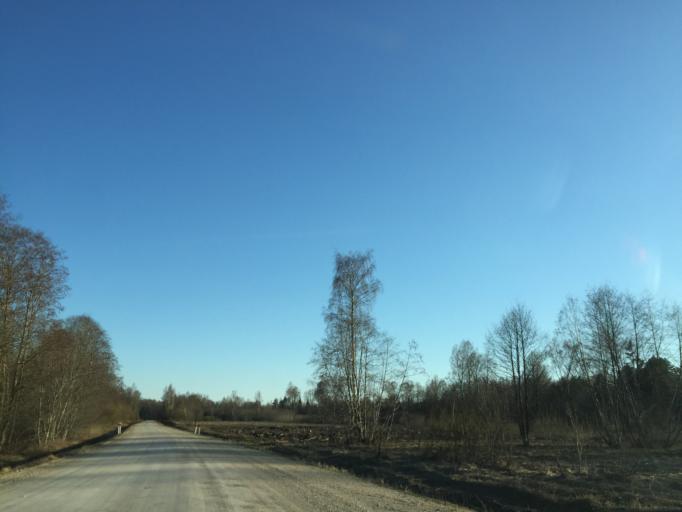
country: EE
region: Ida-Virumaa
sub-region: Sillamaee linn
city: Sillamae
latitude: 59.1113
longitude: 27.7968
